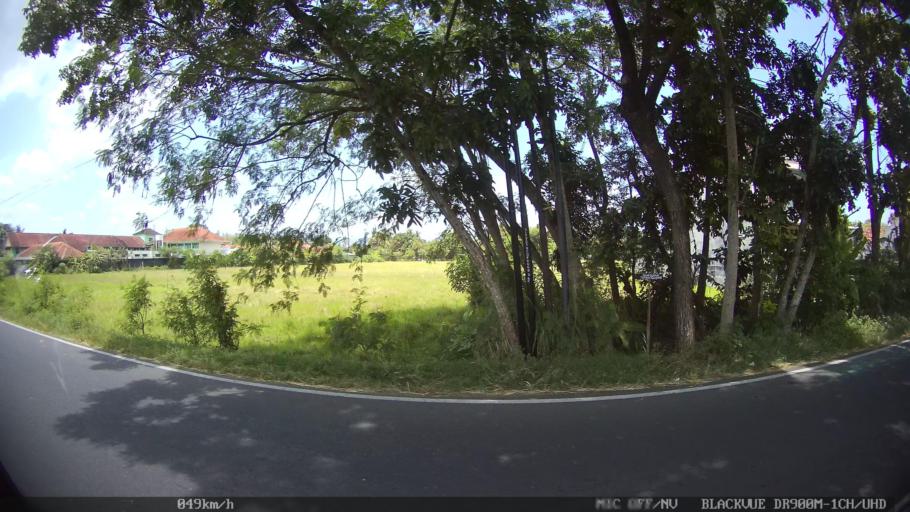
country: ID
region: Daerah Istimewa Yogyakarta
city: Bantul
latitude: -7.9049
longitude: 110.3303
